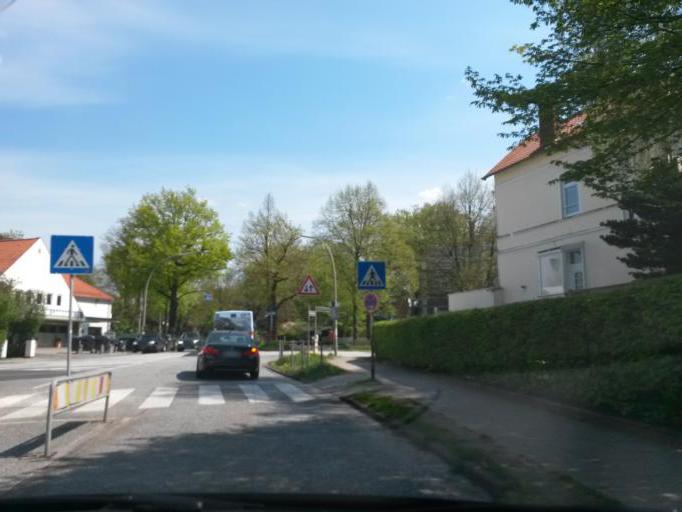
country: DE
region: Hamburg
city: Eidelstedt
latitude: 53.5653
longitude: 9.8796
